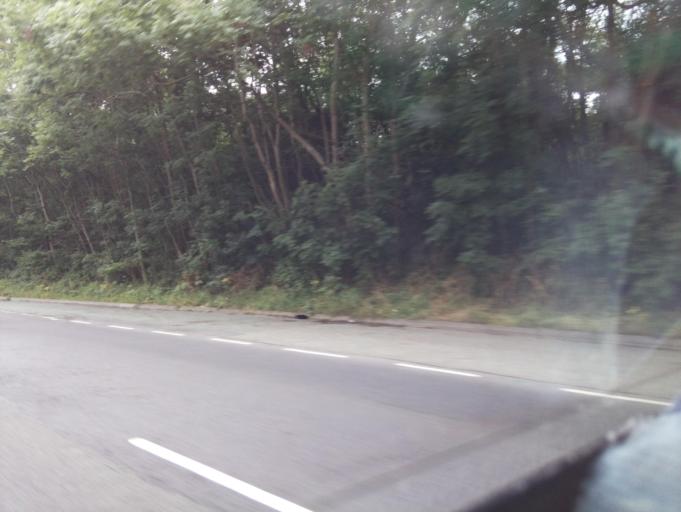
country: GB
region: England
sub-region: Northamptonshire
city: Geddington
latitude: 52.4562
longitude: -0.7366
